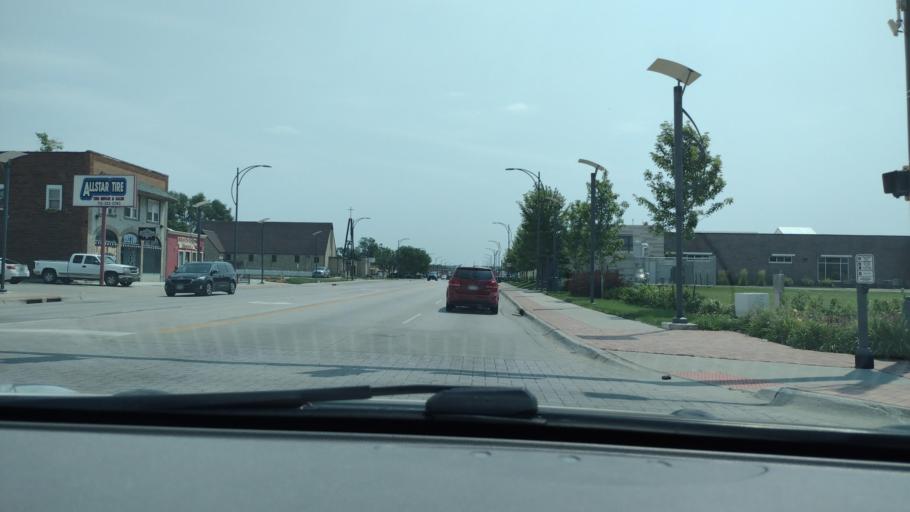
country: US
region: Iowa
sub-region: Pottawattamie County
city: Council Bluffs
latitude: 41.2619
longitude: -95.8964
